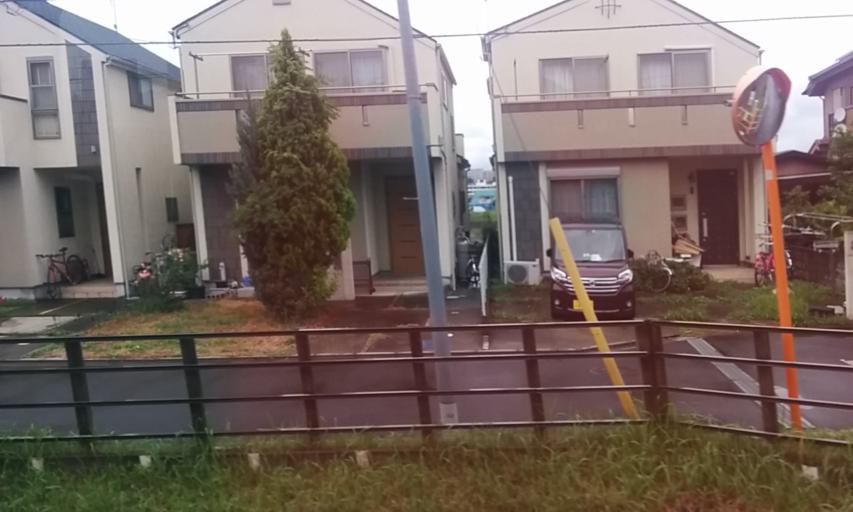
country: JP
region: Tokyo
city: Hino
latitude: 35.6452
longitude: 139.3776
